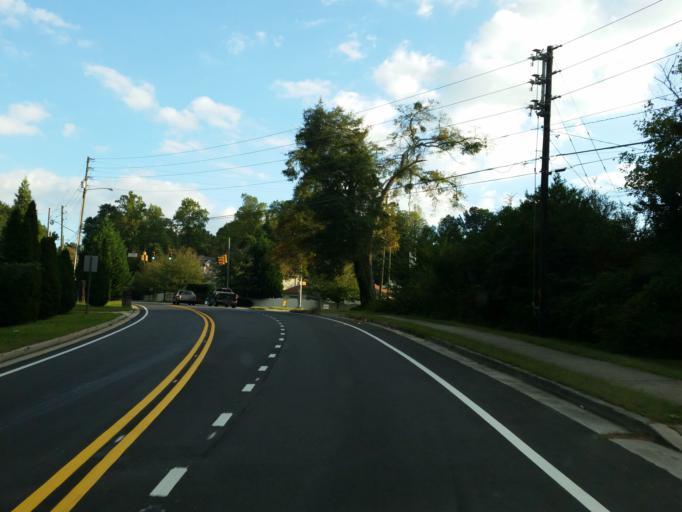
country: US
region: Georgia
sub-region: Cobb County
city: Smyrna
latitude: 33.8769
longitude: -84.5397
